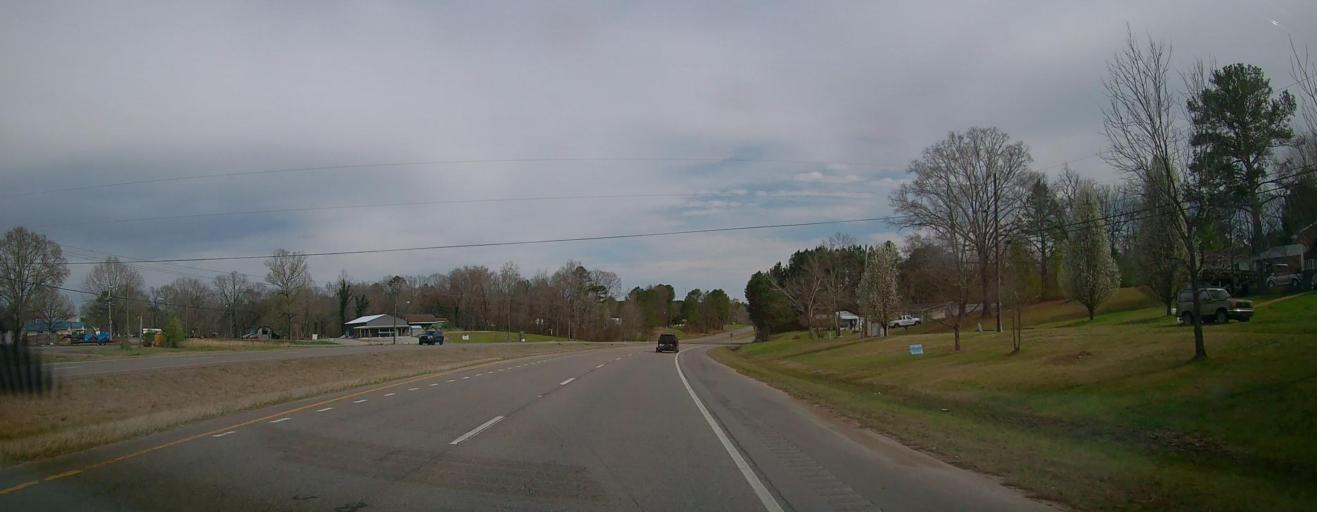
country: US
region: Alabama
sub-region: Walker County
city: Sumiton
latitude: 33.7920
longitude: -87.0934
